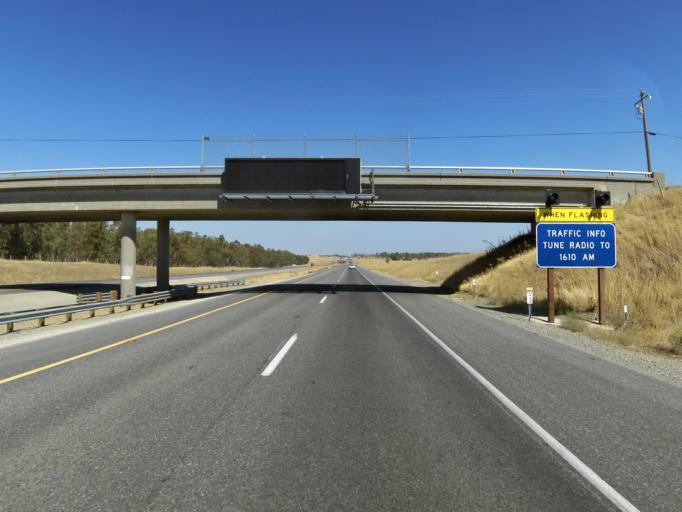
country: US
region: California
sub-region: Tehama County
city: Corning
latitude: 39.8485
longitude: -122.1999
